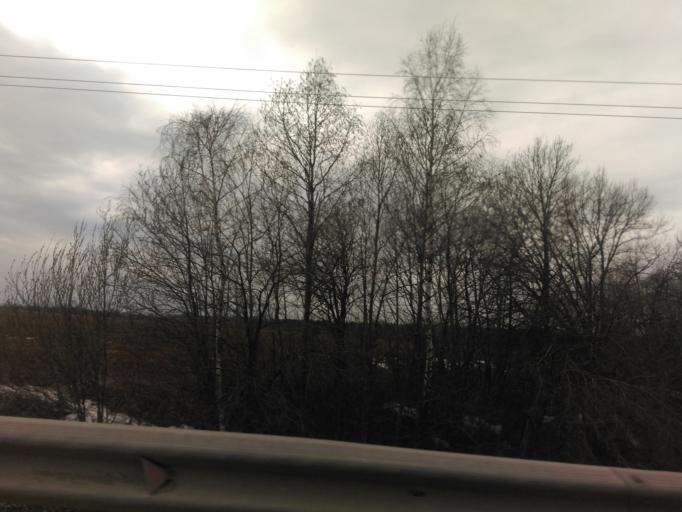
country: RU
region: Moskovskaya
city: Zvenigorod
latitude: 55.7478
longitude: 36.9358
